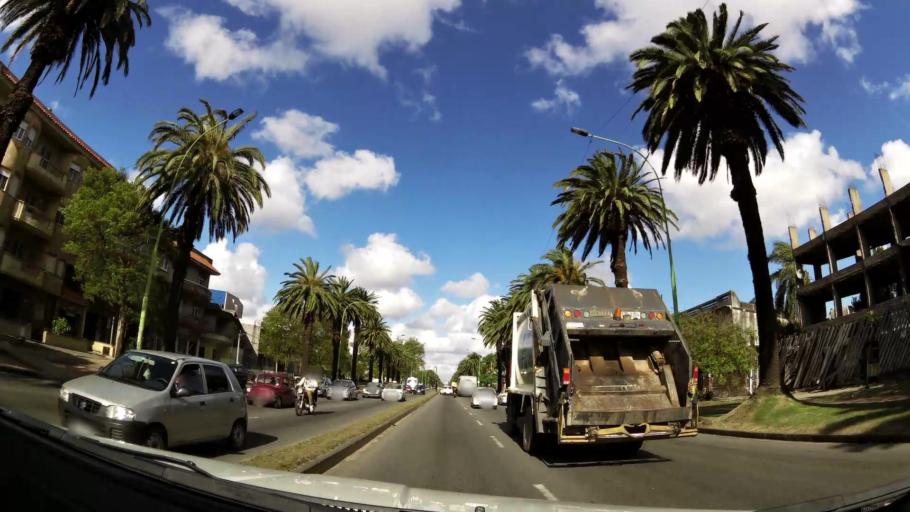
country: UY
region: Montevideo
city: Montevideo
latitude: -34.8714
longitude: -56.1896
